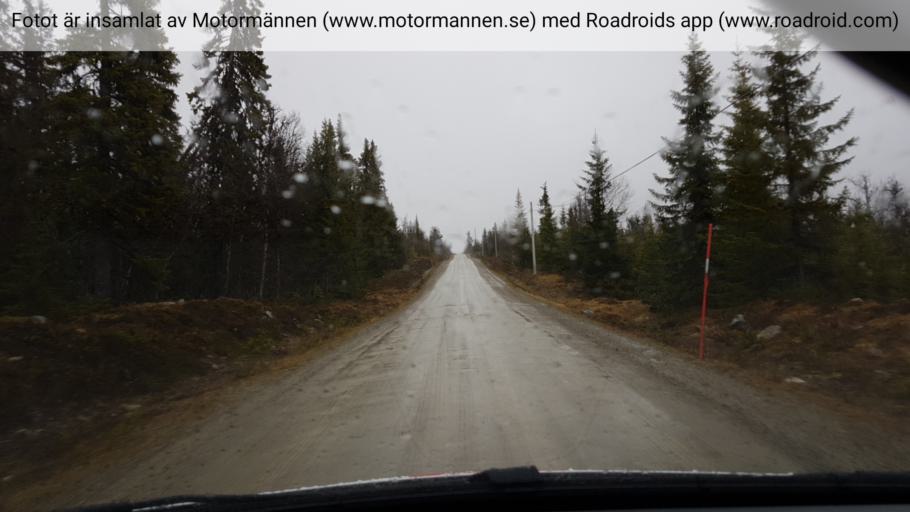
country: SE
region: Jaemtland
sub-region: Are Kommun
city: Jarpen
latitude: 62.6008
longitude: 13.2767
